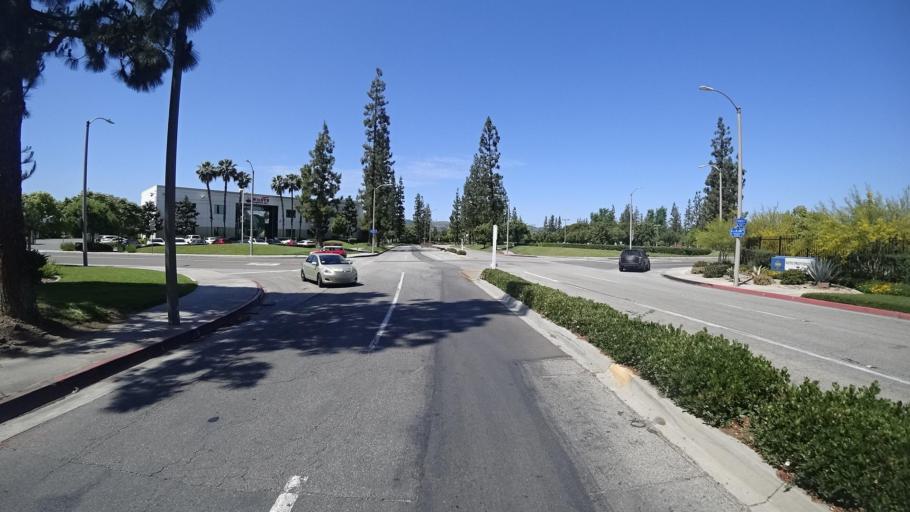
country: US
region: California
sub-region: Los Angeles County
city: La Puente
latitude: 34.0178
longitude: -117.9615
